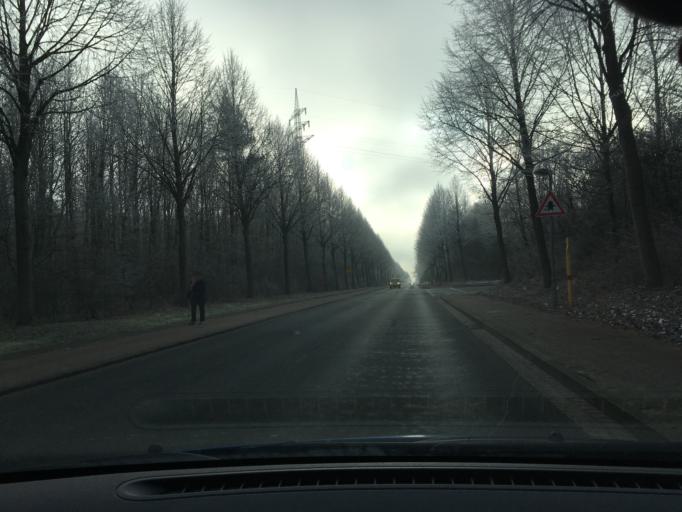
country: DE
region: Lower Saxony
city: Bardowick
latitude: 53.2701
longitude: 10.3887
